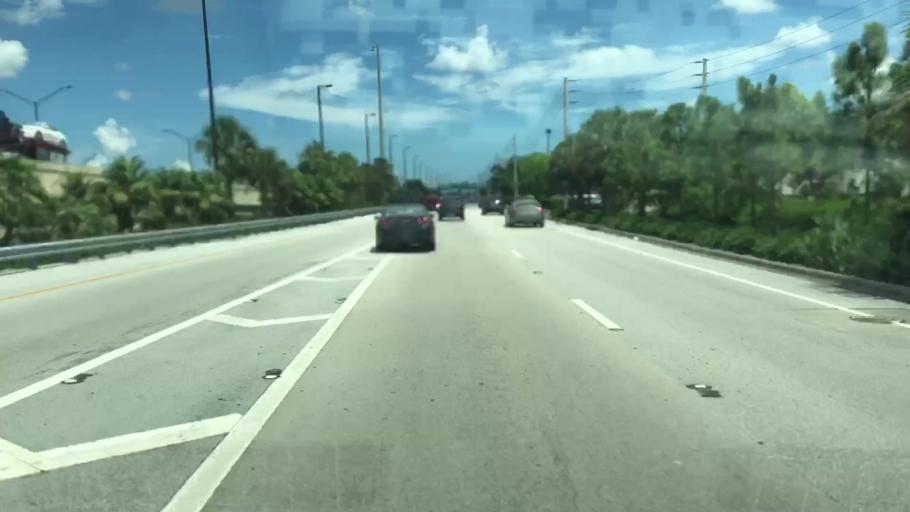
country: US
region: Florida
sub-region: Broward County
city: Pine Island Ridge
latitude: 26.1006
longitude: -80.2622
